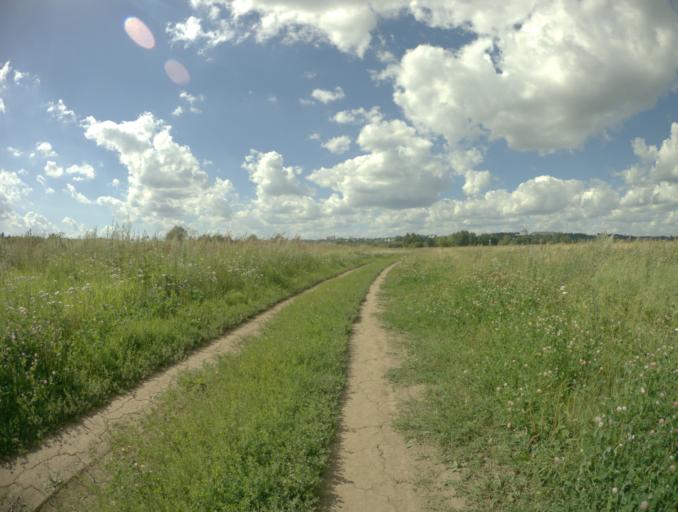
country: RU
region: Vladimir
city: Kommunar
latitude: 56.1145
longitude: 40.4270
